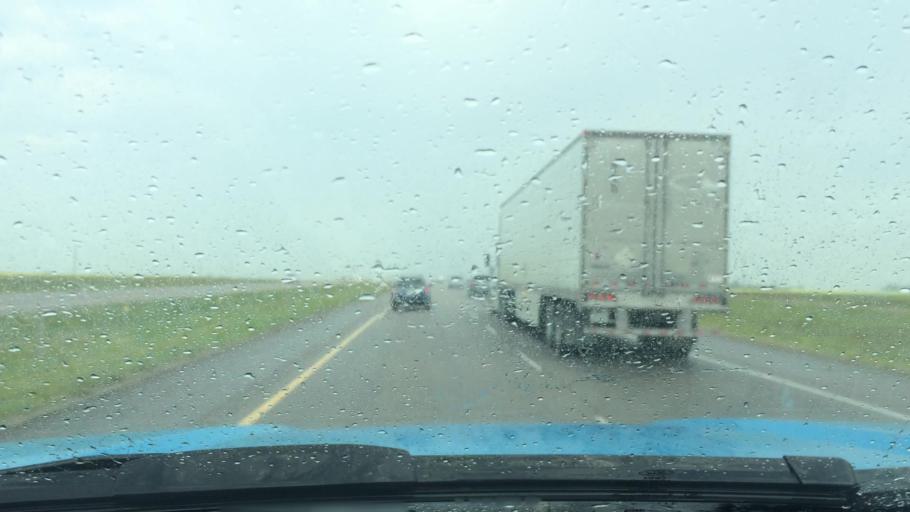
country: CA
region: Alberta
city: Carstairs
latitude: 51.6060
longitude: -114.0253
